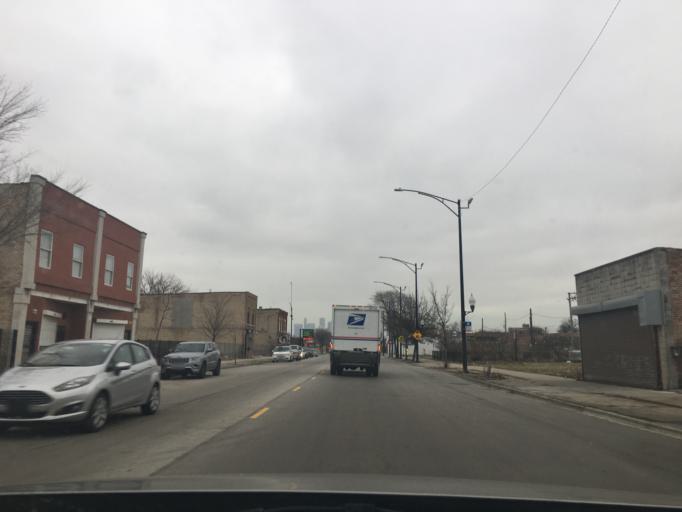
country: US
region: Illinois
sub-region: Cook County
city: Chicago
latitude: 41.8810
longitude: -87.7003
